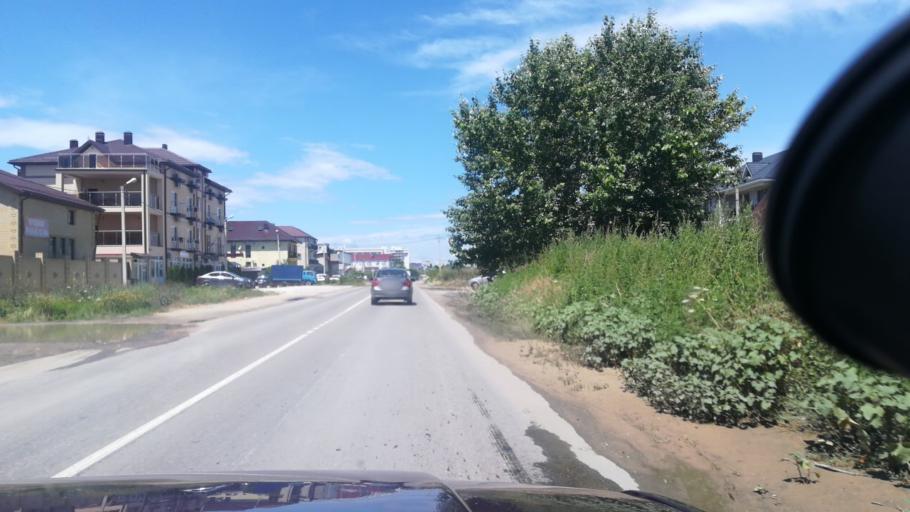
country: RU
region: Krasnodarskiy
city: Vityazevo
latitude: 44.9607
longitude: 37.2946
